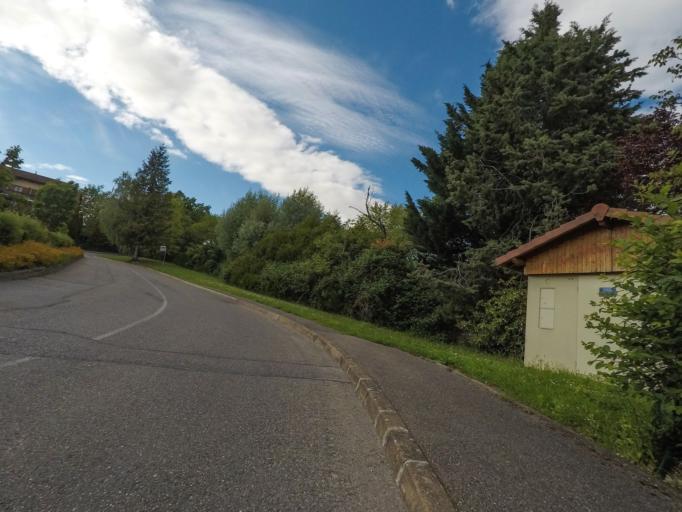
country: CH
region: Geneva
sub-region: Geneva
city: Meyrin
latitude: 46.2510
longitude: 6.0842
